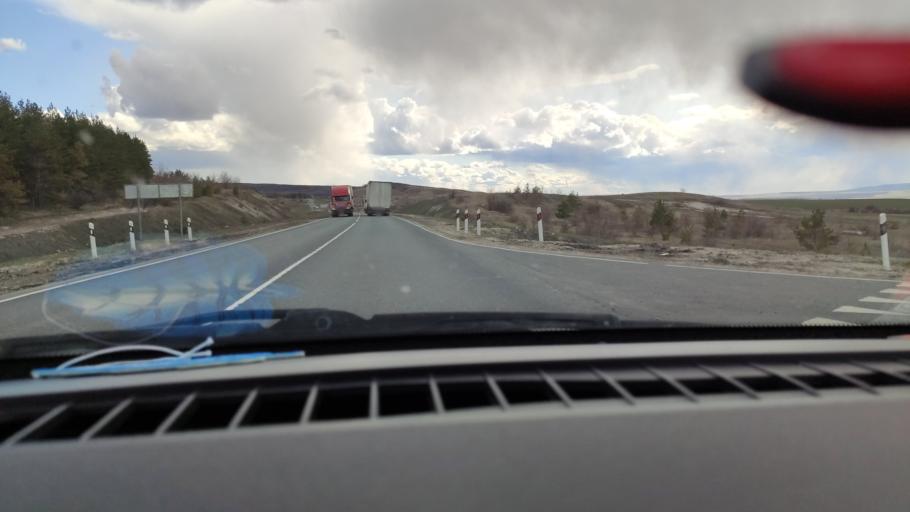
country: RU
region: Saratov
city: Alekseyevka
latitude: 52.3830
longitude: 47.9733
